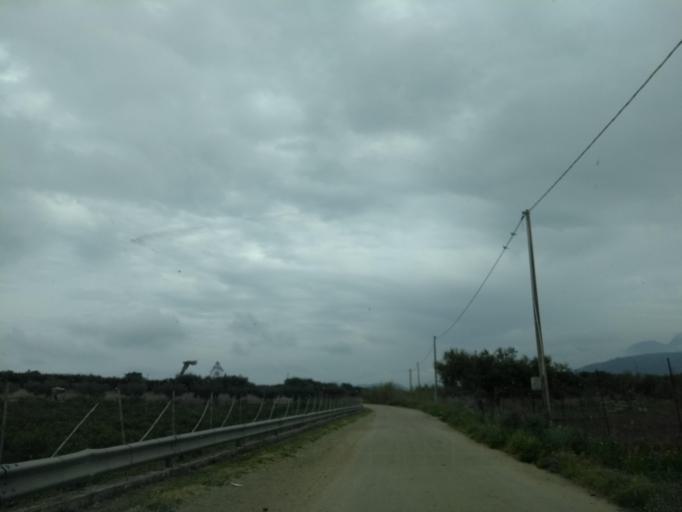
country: IT
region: Sicily
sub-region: Palermo
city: Partinico
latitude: 37.9934
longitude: 13.0760
